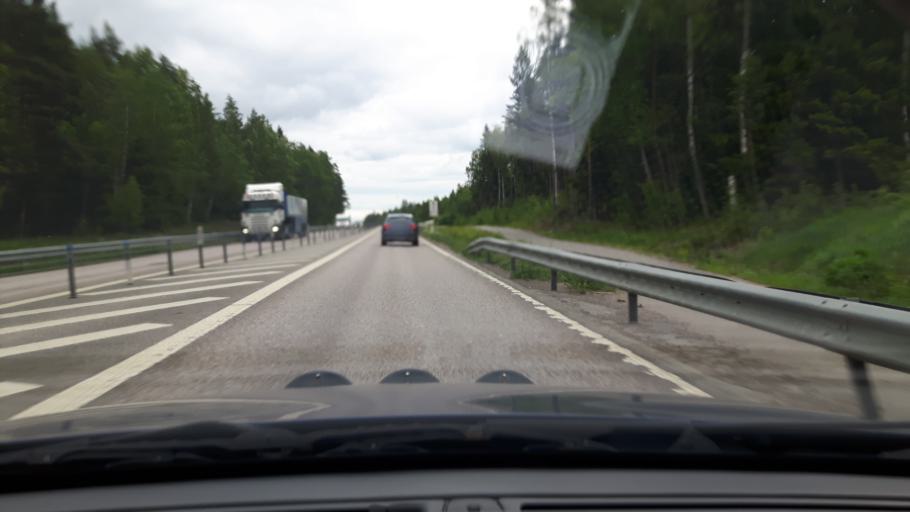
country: SE
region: Soedermanland
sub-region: Katrineholms Kommun
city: Katrineholm
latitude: 59.0112
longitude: 16.2639
